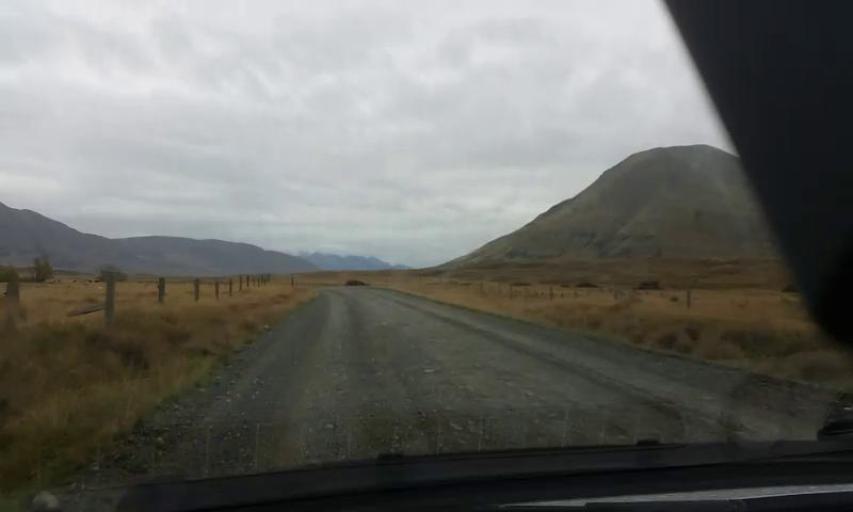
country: NZ
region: Canterbury
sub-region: Ashburton District
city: Methven
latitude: -43.6143
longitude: 171.1194
